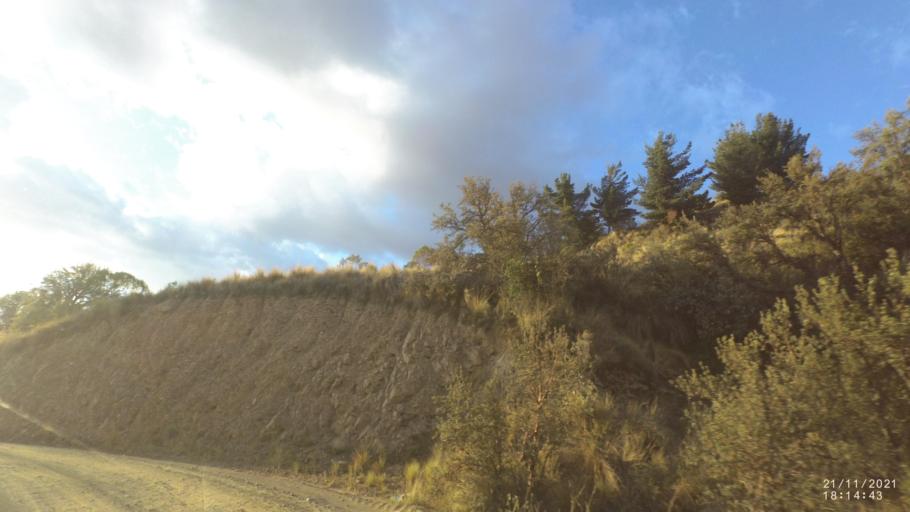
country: BO
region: Cochabamba
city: Cochabamba
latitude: -17.2884
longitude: -66.2117
